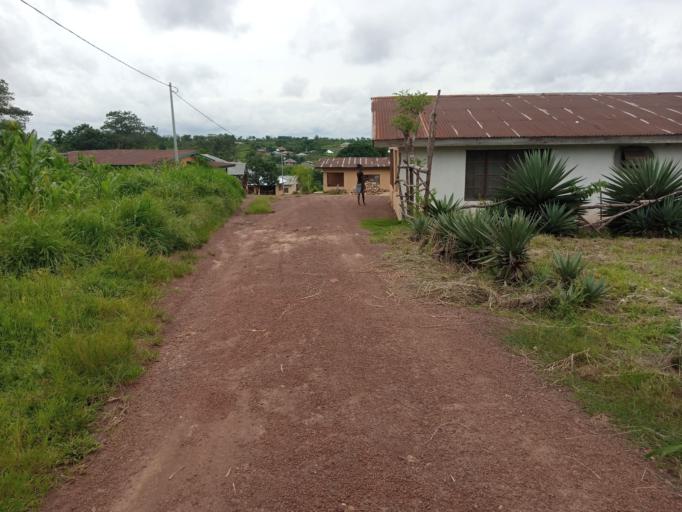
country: SL
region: Southern Province
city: Largo
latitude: 8.2002
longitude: -12.0582
